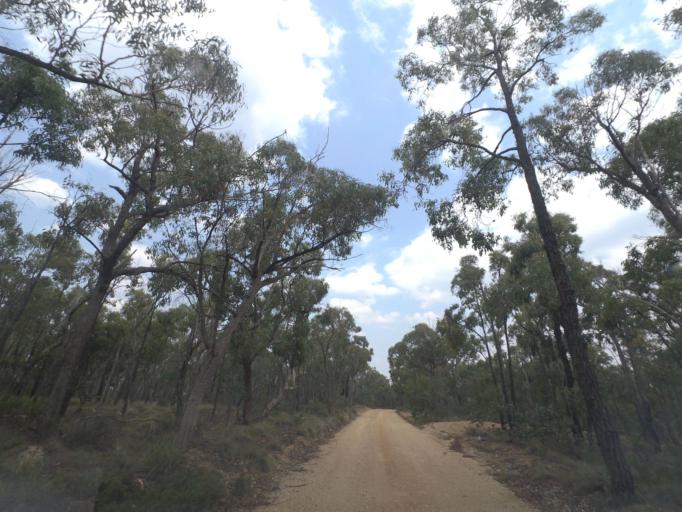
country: AU
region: Victoria
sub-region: Moorabool
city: Bacchus Marsh
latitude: -37.5785
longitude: 144.4412
